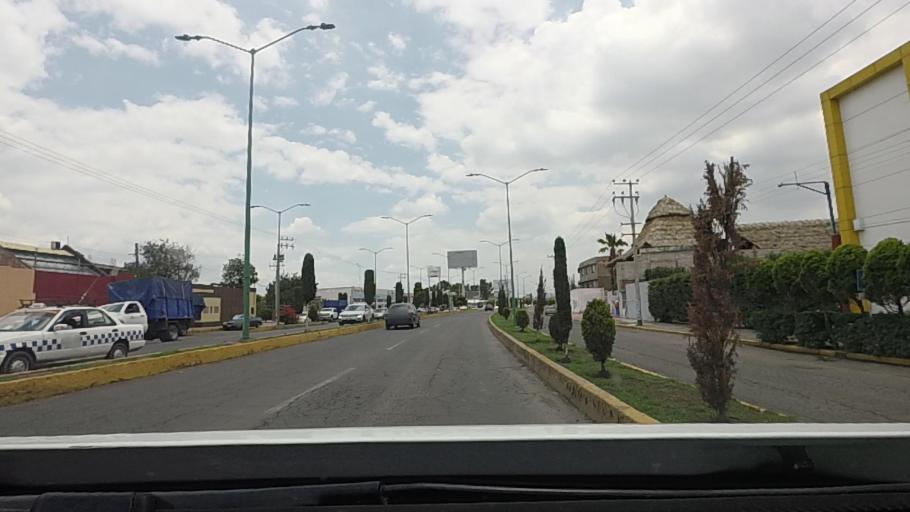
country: MX
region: Mexico
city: Chalco de Diaz Covarrubias
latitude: 19.2543
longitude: -98.8843
